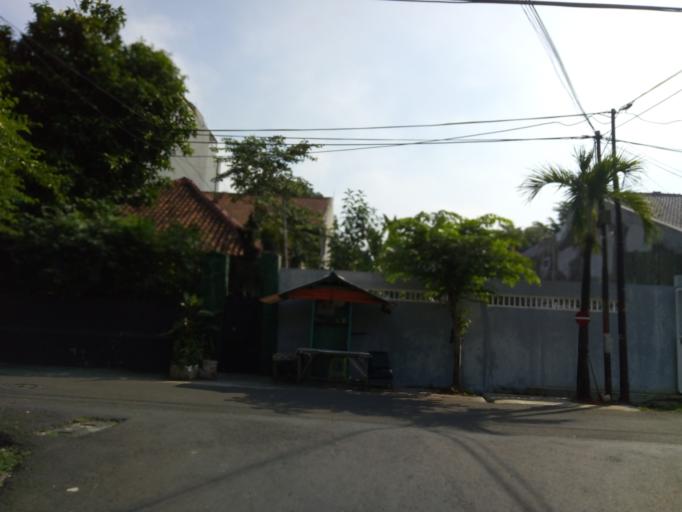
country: ID
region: Jakarta Raya
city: Jakarta
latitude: -6.2064
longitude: 106.8353
